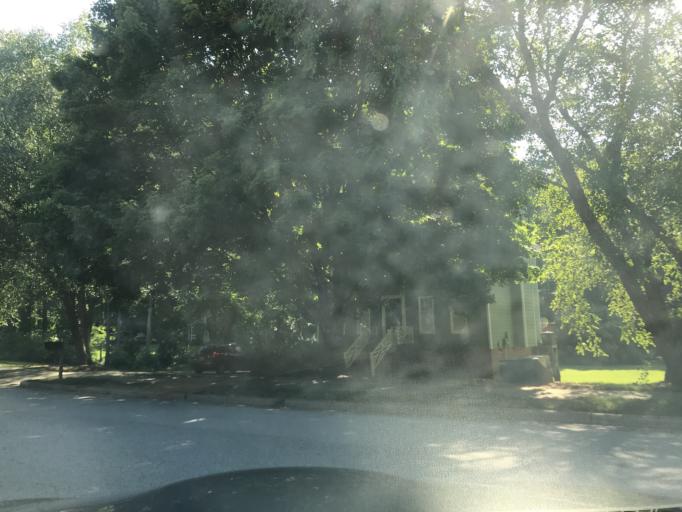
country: US
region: North Carolina
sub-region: Wake County
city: West Raleigh
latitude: 35.8576
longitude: -78.6070
